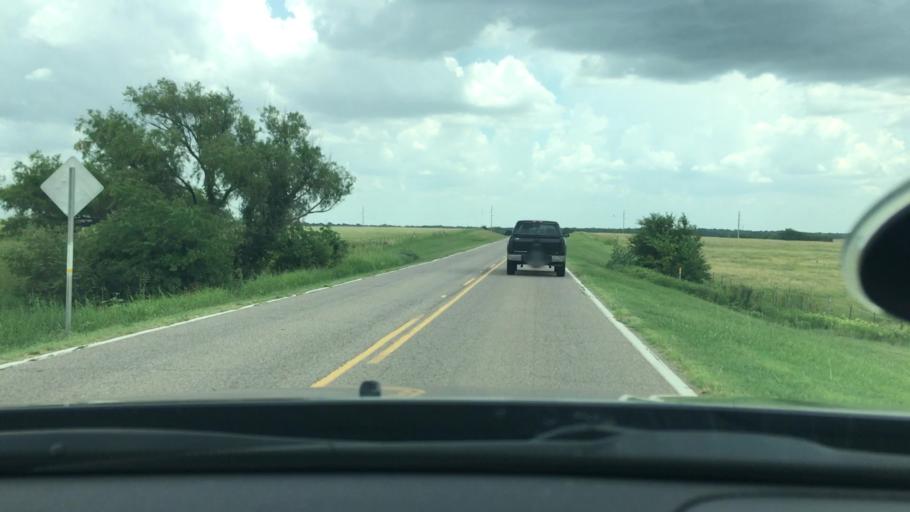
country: US
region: Oklahoma
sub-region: Marshall County
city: Oakland
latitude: 34.0709
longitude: -96.8042
